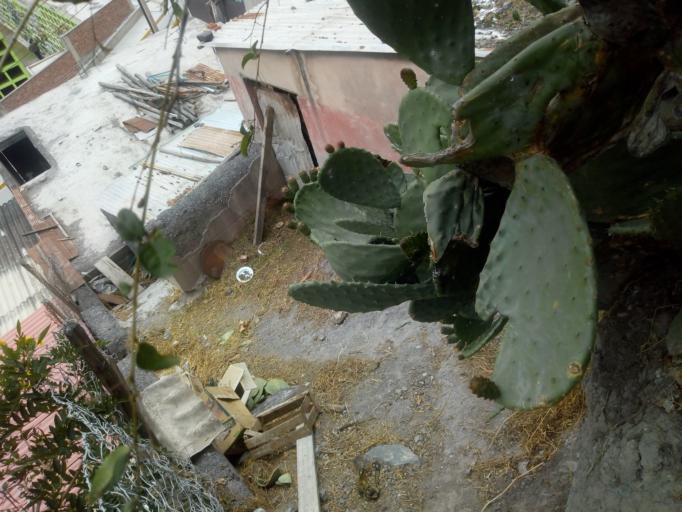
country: PE
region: Lima
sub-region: Provincia de Huarochiri
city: Matucana
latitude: -11.8422
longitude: -76.3795
